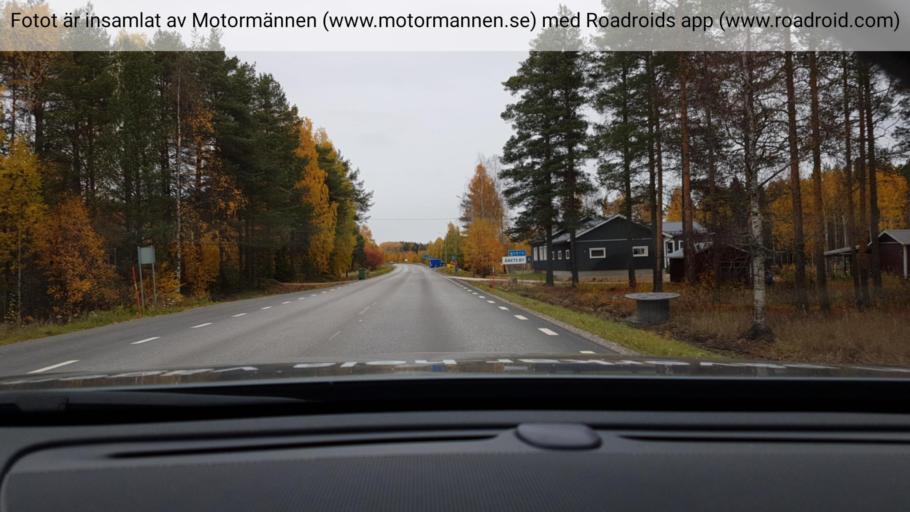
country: SE
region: Norrbotten
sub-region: Overkalix Kommun
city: OEverkalix
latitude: 66.3596
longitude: 22.8350
